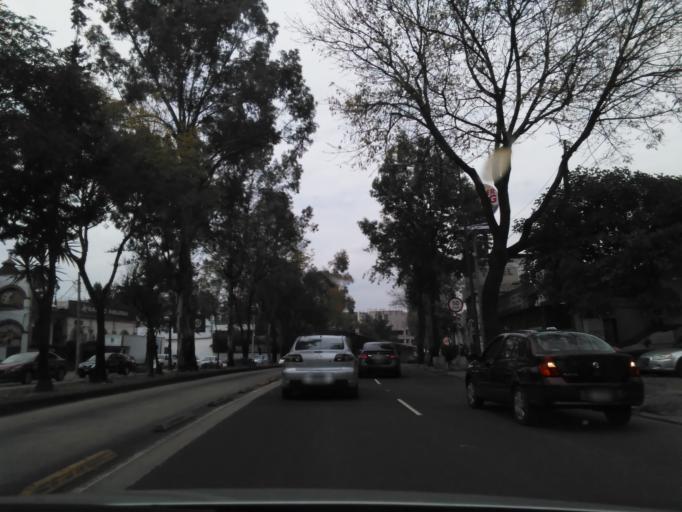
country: MX
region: Mexico City
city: Tlalpan
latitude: 19.2825
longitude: -99.1745
